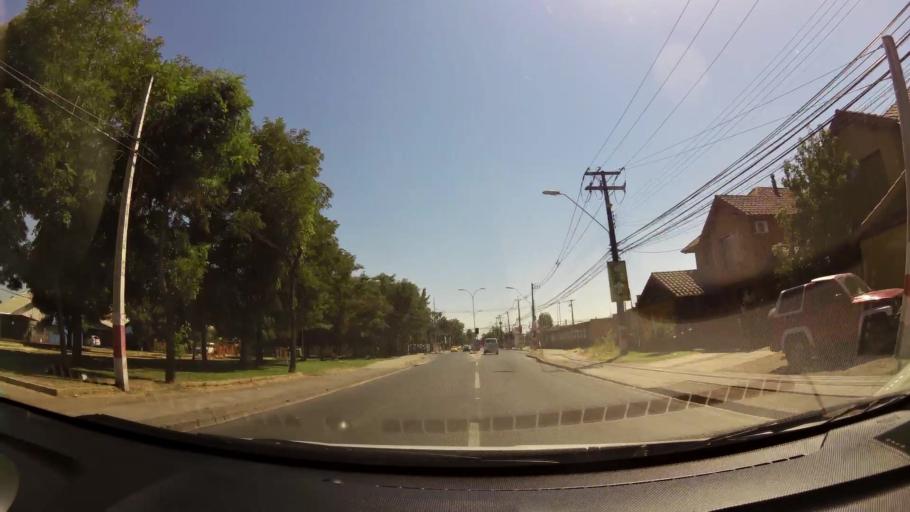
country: CL
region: Maule
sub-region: Provincia de Curico
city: Curico
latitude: -34.9713
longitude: -71.2309
